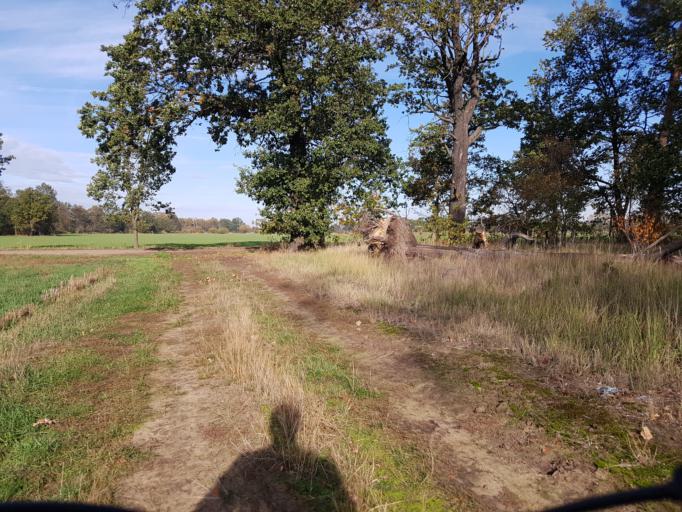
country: DE
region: Brandenburg
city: Schilda
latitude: 51.5962
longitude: 13.3319
